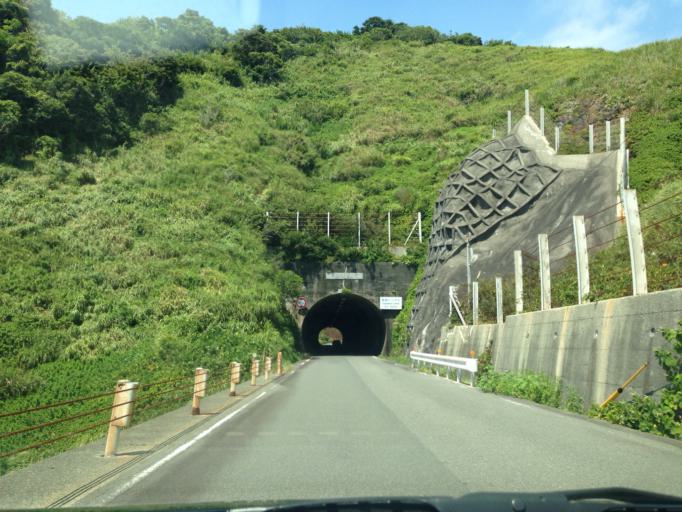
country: JP
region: Shizuoka
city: Shimoda
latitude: 34.6105
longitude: 138.8269
